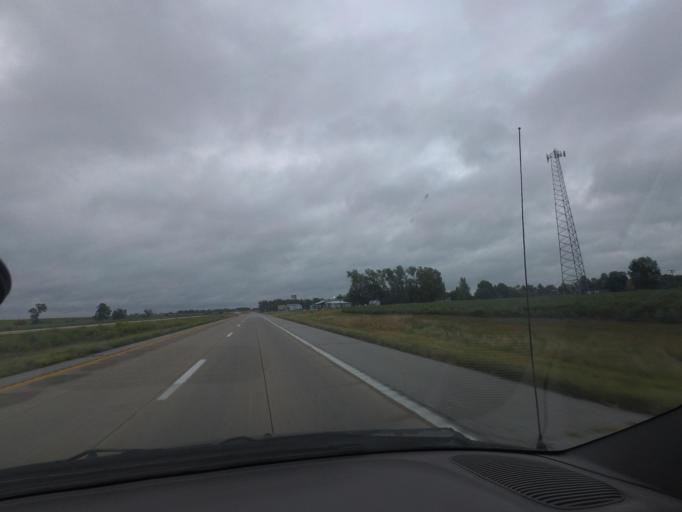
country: US
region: Missouri
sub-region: Marion County
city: Monroe City
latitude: 39.6696
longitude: -91.8543
